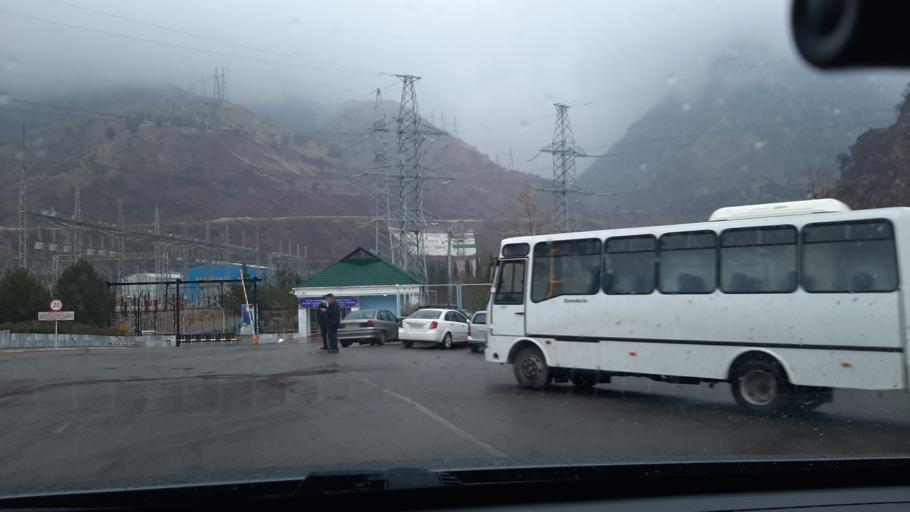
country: TJ
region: Khatlon
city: Norak
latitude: 38.3815
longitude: 69.3476
